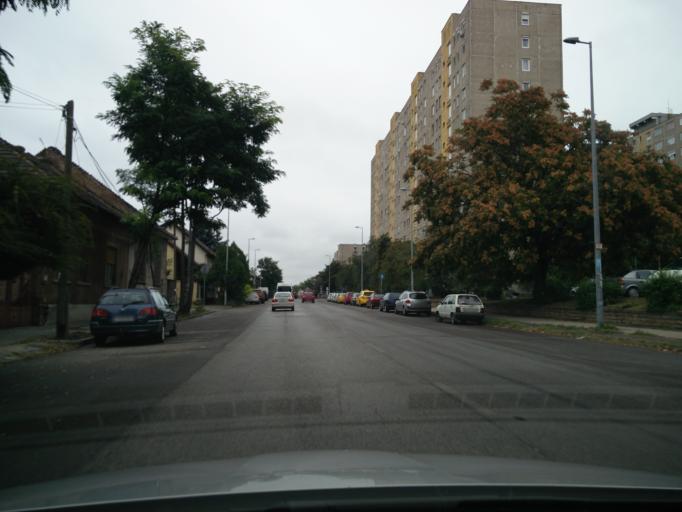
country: HU
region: Budapest
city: Budapest XIX. keruelet
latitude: 47.4584
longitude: 19.1479
